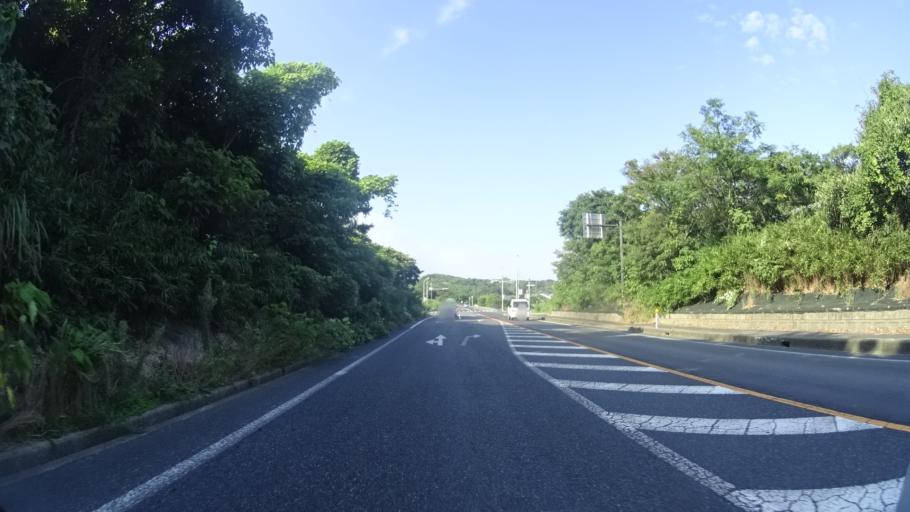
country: JP
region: Shimane
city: Izumo
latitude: 35.3175
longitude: 132.6642
